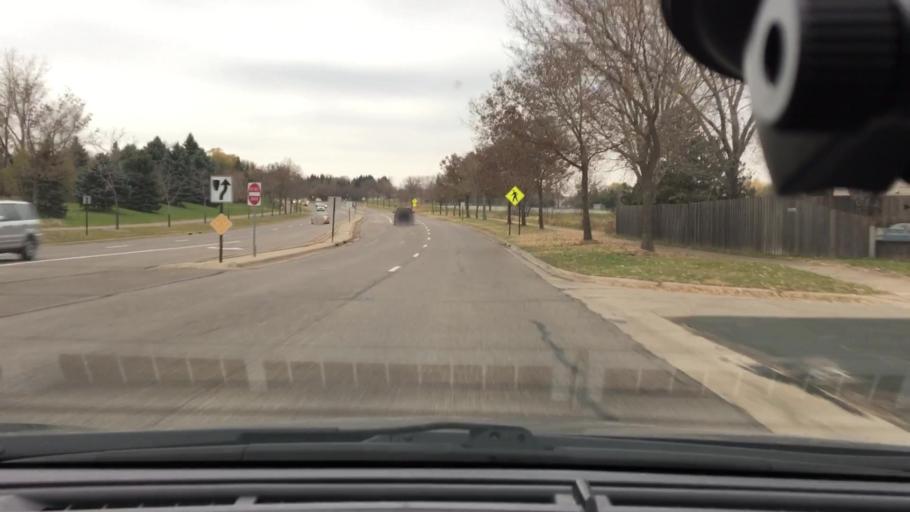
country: US
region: Minnesota
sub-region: Hennepin County
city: Osseo
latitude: 45.1211
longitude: -93.4494
